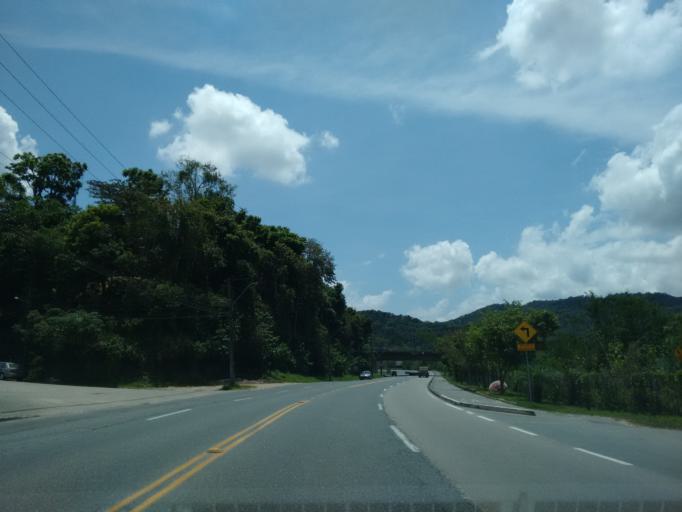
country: BR
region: Santa Catarina
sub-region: Blumenau
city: Blumenau
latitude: -26.9031
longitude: -49.0461
